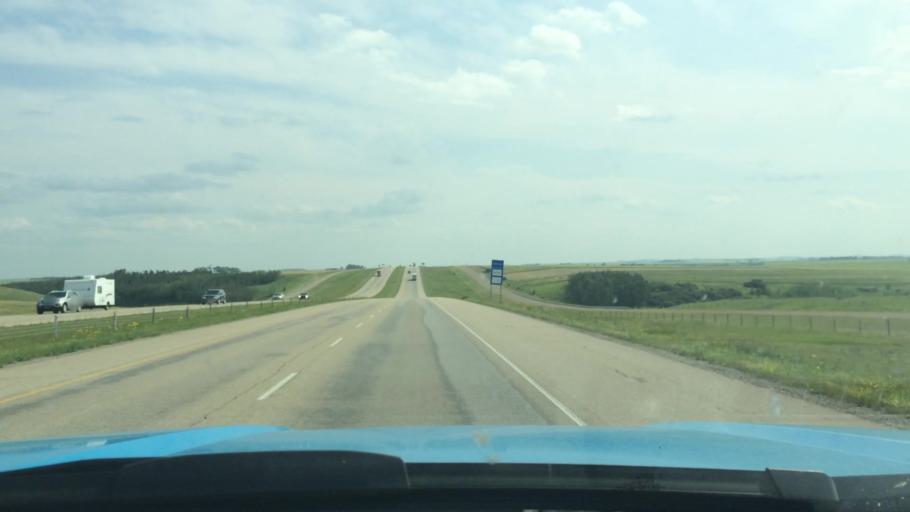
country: CA
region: Alberta
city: Carstairs
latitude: 51.5816
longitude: -114.0253
